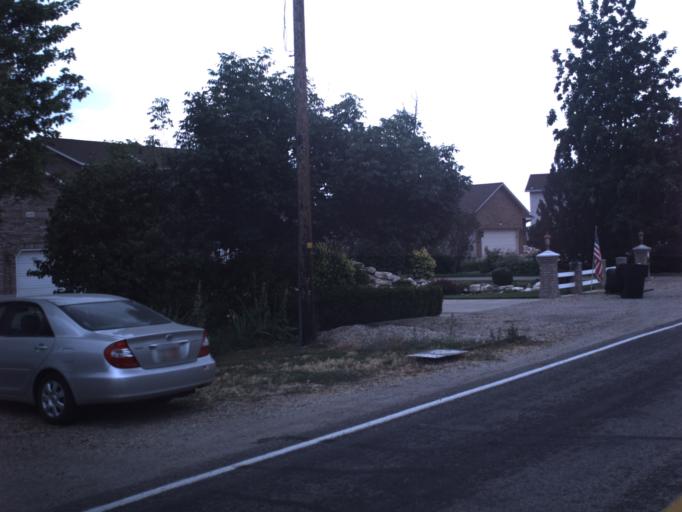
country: US
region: Utah
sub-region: Davis County
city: West Point
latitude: 41.0903
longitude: -112.1128
